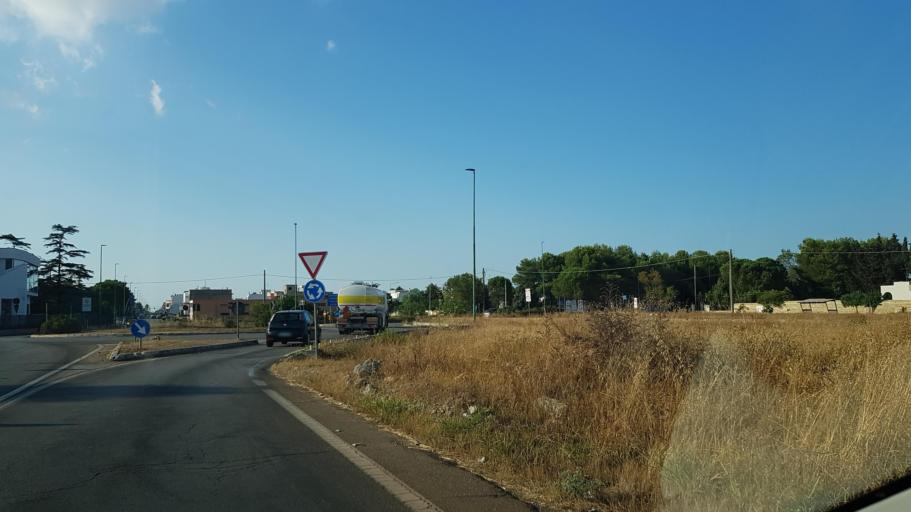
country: IT
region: Apulia
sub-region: Provincia di Lecce
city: Montesano Salentino
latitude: 39.9726
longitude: 18.3263
